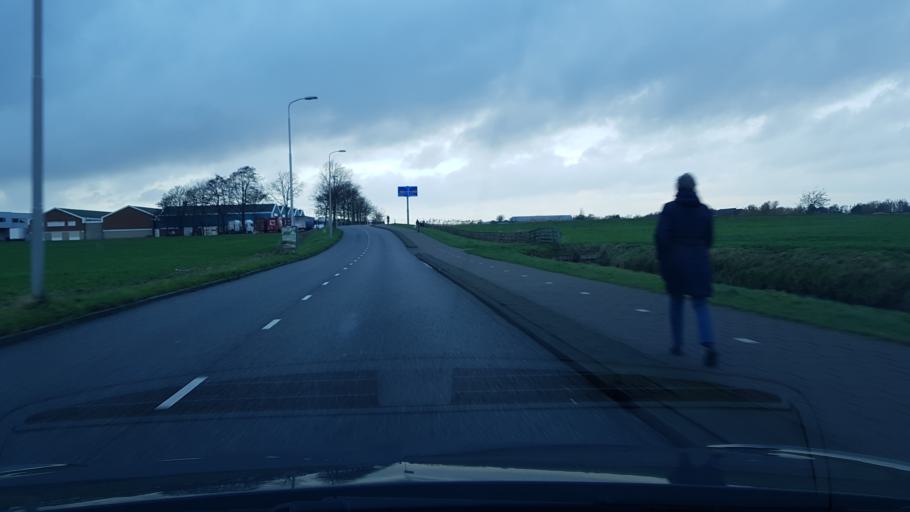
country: NL
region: South Holland
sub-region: Gemeente Lisse
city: Lisse
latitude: 52.2420
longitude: 4.5471
